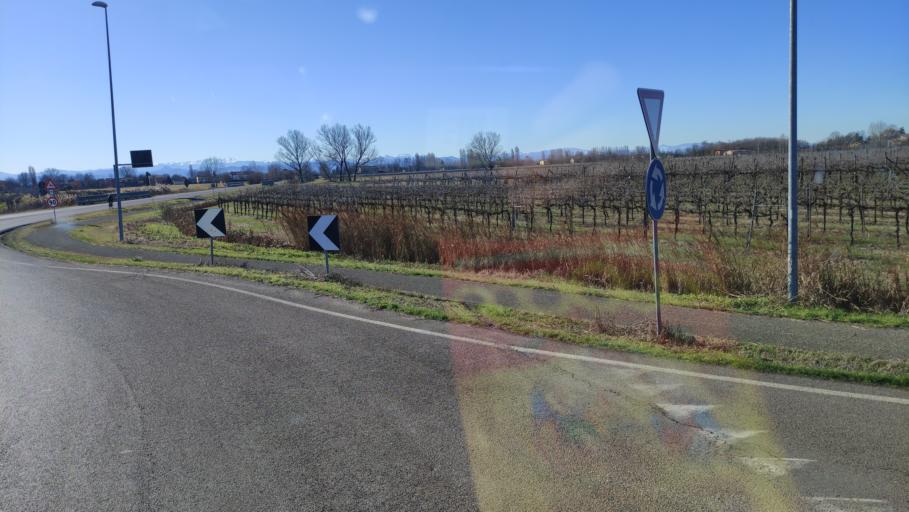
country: IT
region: Emilia-Romagna
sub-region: Provincia di Reggio Emilia
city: San Martino in Rio
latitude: 44.7424
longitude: 10.7747
